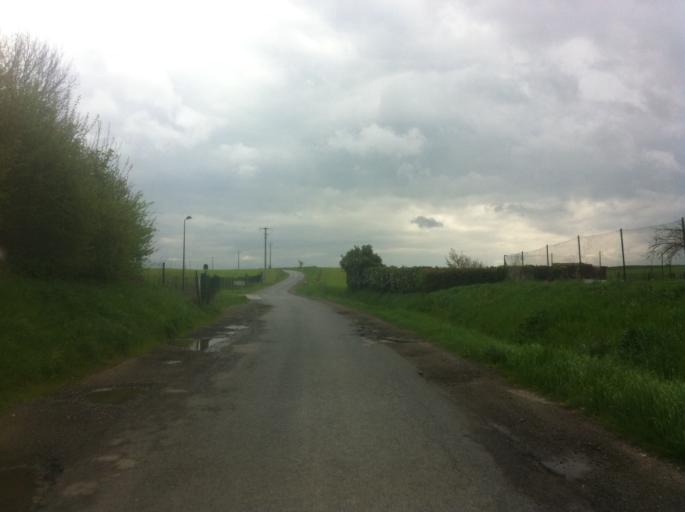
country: FR
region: Picardie
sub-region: Departement de l'Oise
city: Nanteuil-le-Haudouin
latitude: 49.1356
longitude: 2.8037
